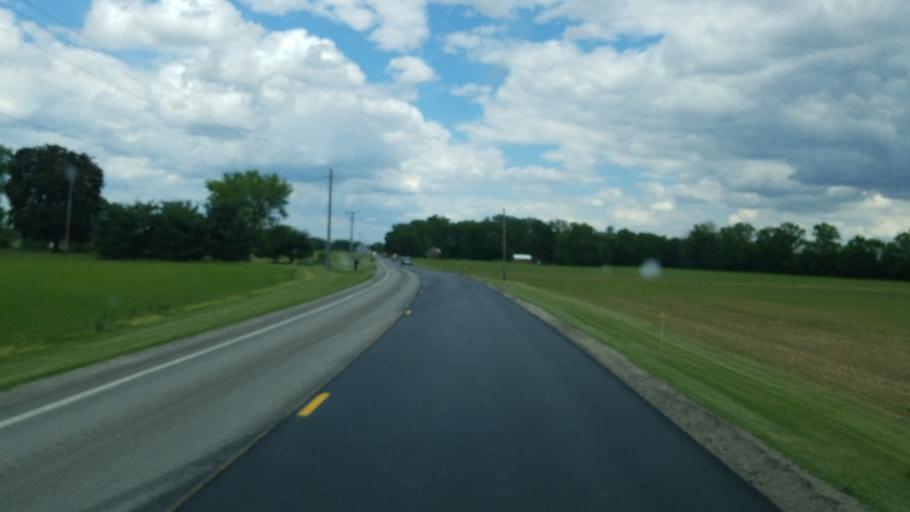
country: US
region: Ohio
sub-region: Erie County
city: Milan
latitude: 41.2985
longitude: -82.6311
